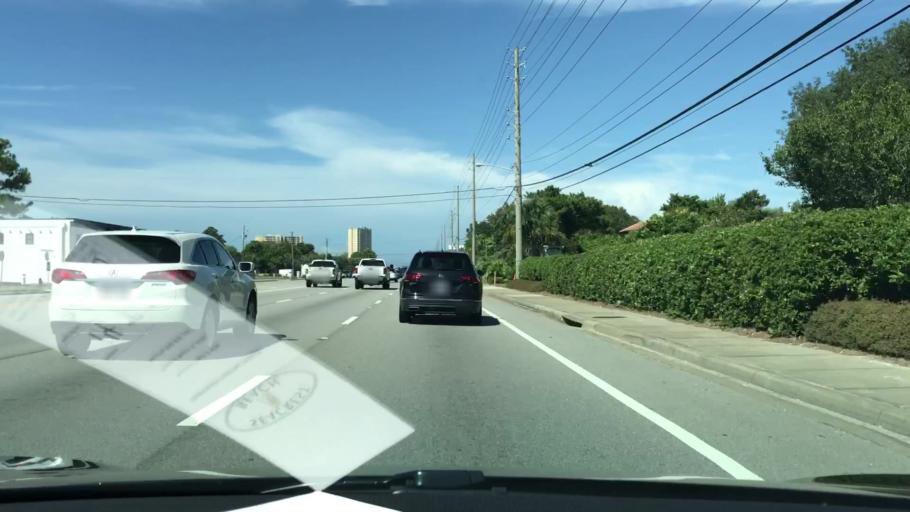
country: US
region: Florida
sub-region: Walton County
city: Miramar Beach
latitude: 30.3762
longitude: -86.3366
